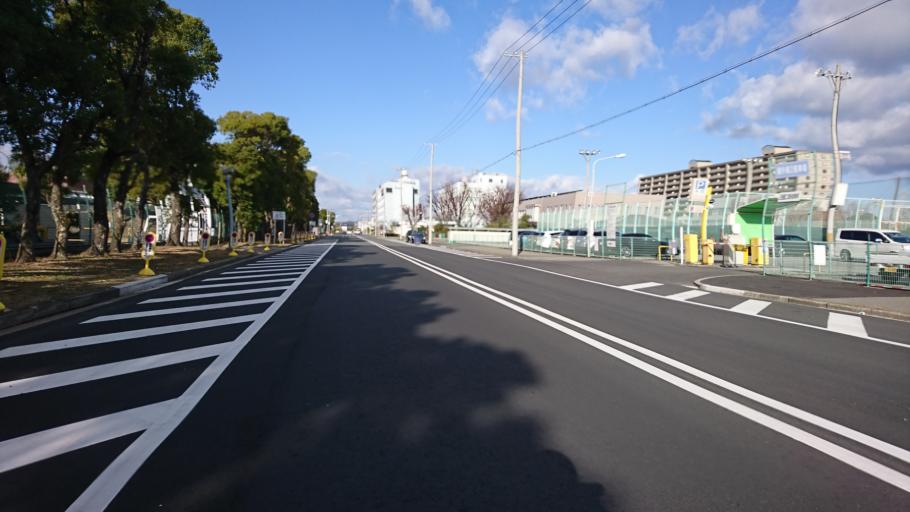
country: JP
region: Hyogo
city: Kakogawacho-honmachi
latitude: 34.7536
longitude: 134.7922
